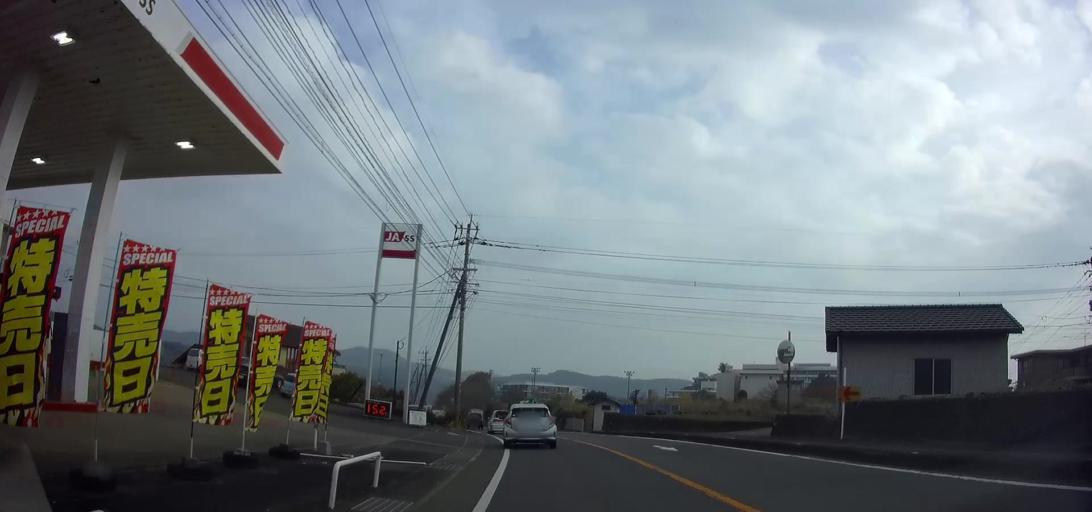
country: JP
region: Nagasaki
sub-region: Isahaya-shi
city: Isahaya
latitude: 32.7916
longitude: 130.0737
